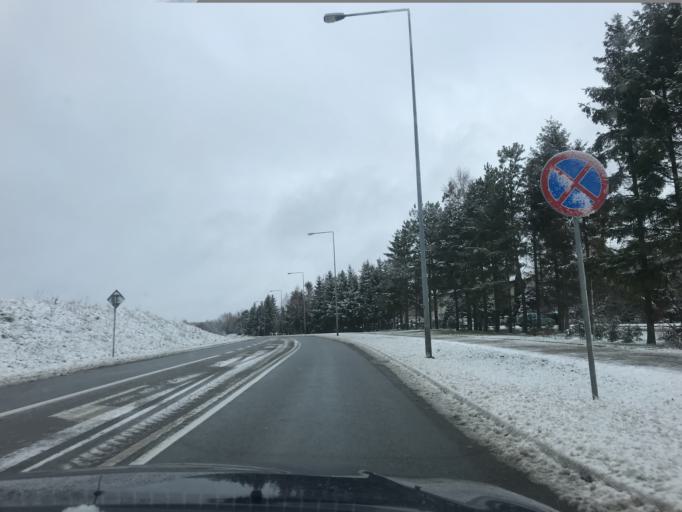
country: PL
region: Pomeranian Voivodeship
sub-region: Powiat bytowski
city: Bytow
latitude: 54.1881
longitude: 17.5097
